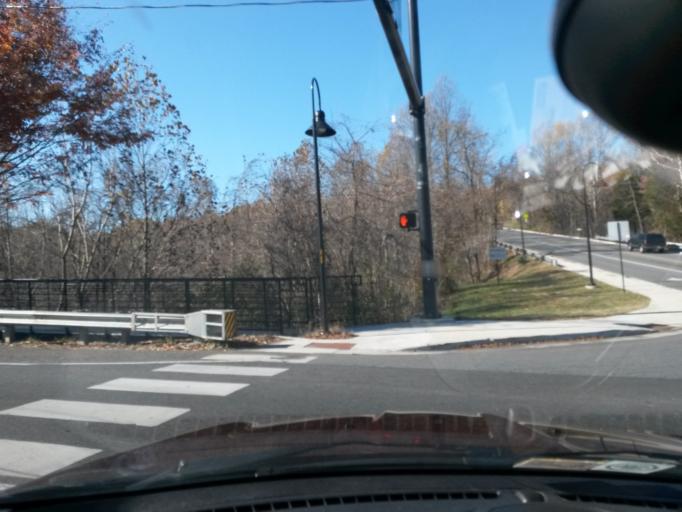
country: US
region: Virginia
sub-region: City of Lynchburg
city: West Lynchburg
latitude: 37.3556
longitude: -79.1820
